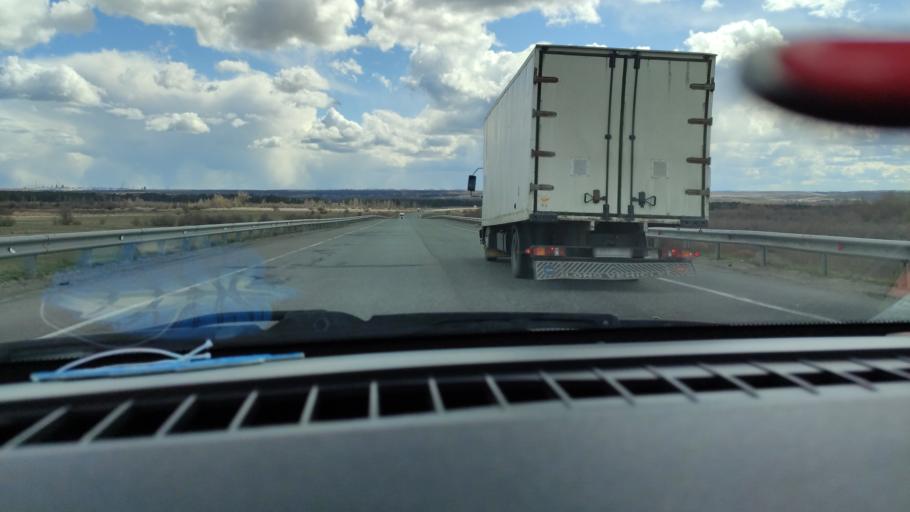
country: RU
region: Samara
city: Varlamovo
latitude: 53.1596
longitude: 48.2839
